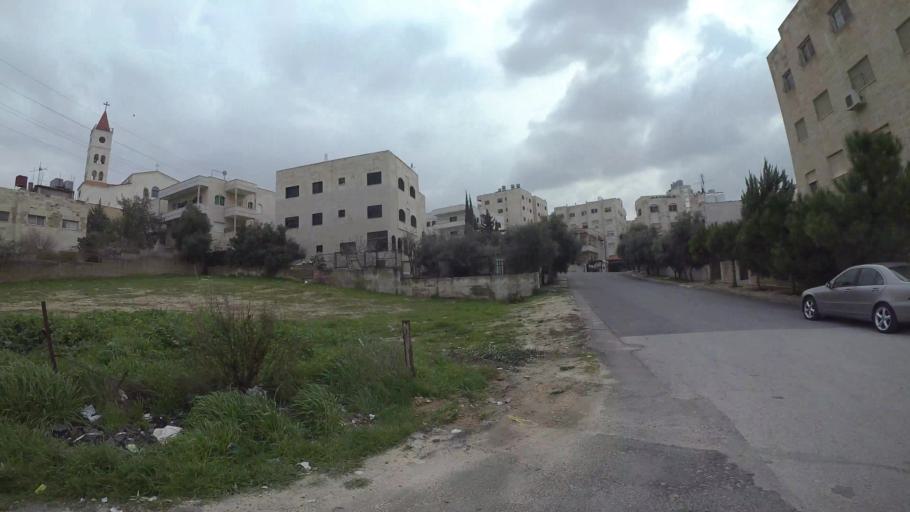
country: JO
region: Amman
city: Umm as Summaq
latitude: 31.8975
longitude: 35.8627
